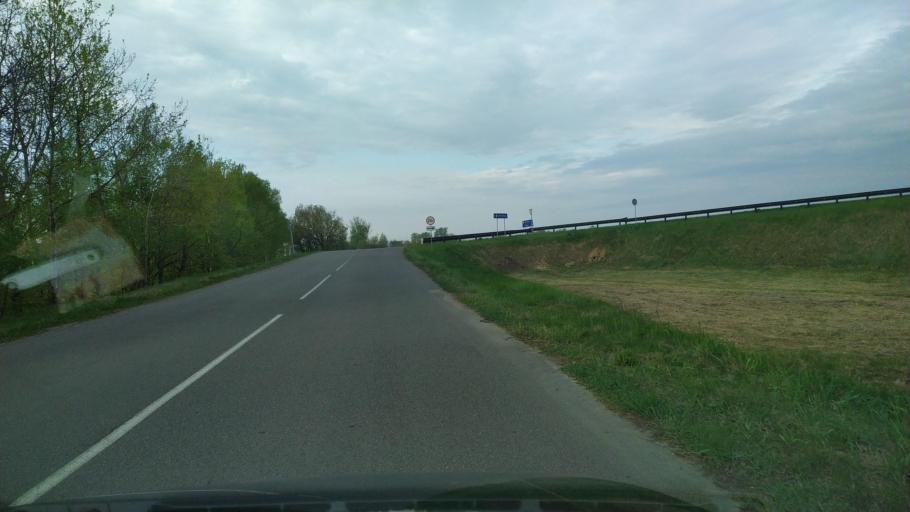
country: BY
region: Brest
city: Zhabinka
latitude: 52.1606
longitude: 24.0869
